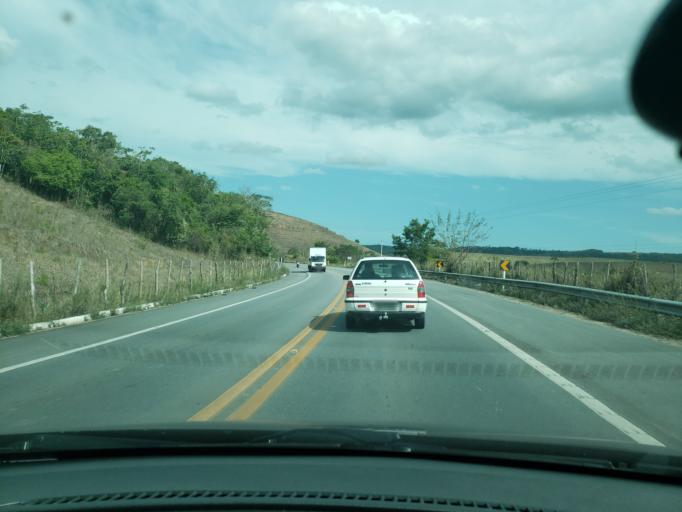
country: BR
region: Alagoas
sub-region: Murici
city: Murici
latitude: -9.3309
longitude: -35.9158
